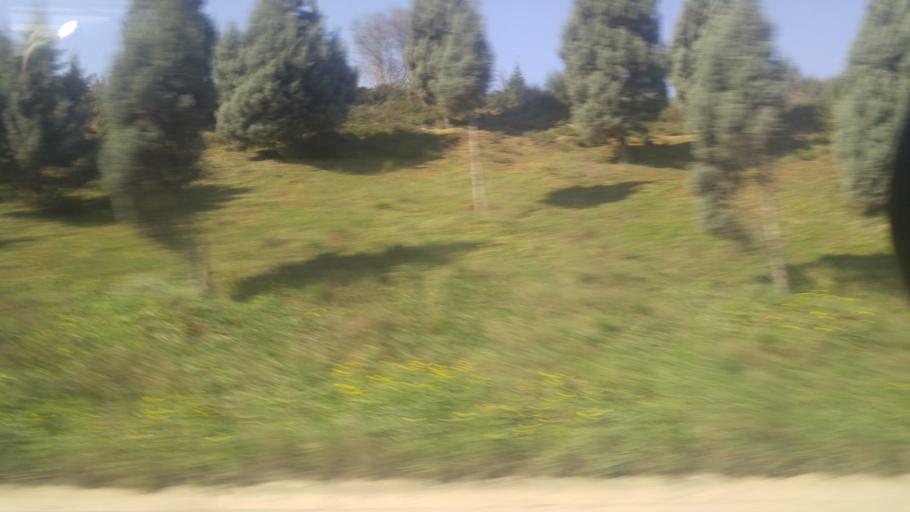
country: TR
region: Kocaeli
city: Balcik
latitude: 40.8490
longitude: 29.3747
